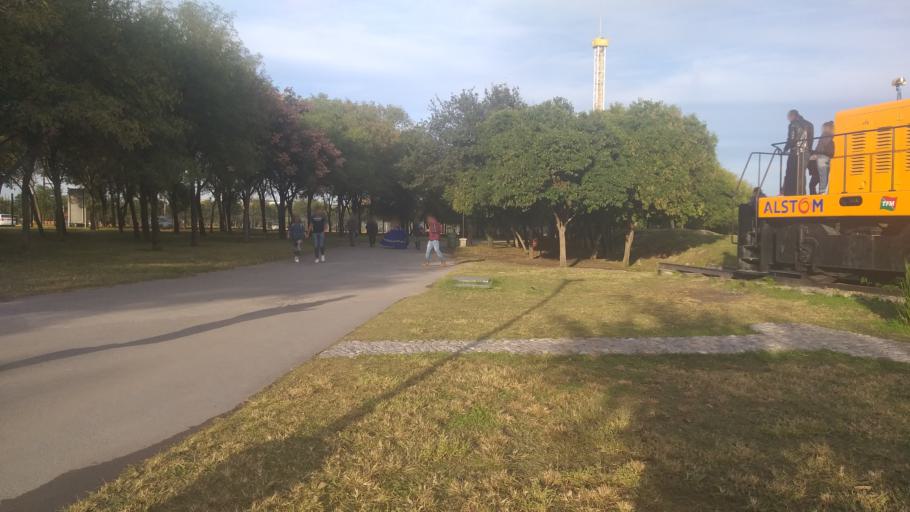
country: MX
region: Nuevo Leon
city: Guadalupe
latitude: 25.6765
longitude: -100.2788
